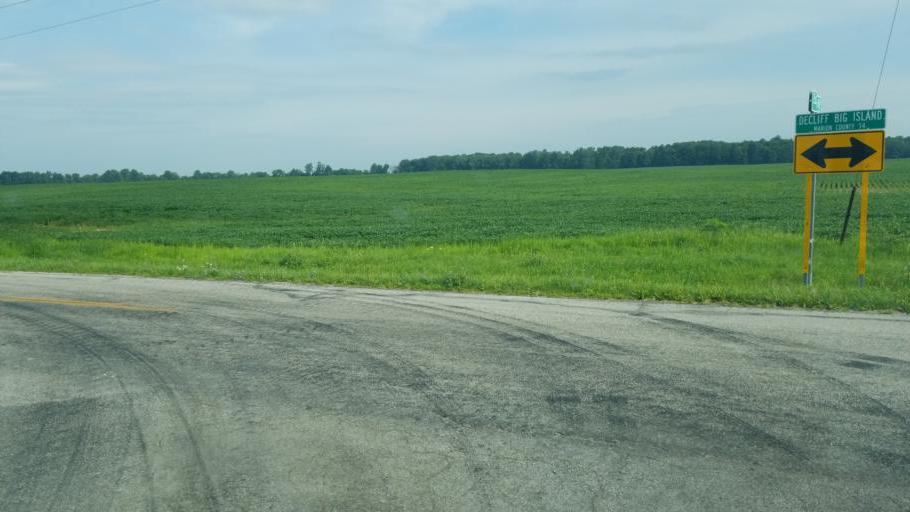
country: US
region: Ohio
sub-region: Marion County
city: Marion
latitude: 40.6079
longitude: -83.2554
